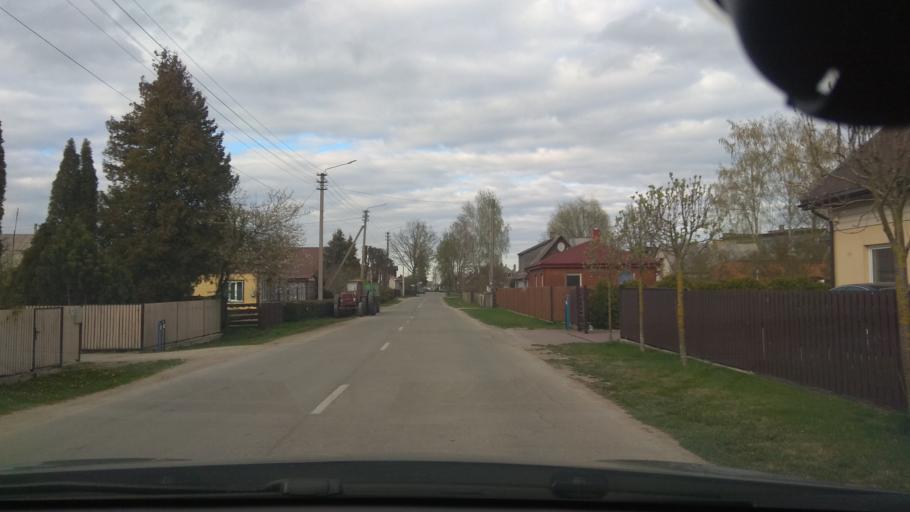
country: LT
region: Siauliu apskritis
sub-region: Joniskis
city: Joniskis
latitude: 56.2465
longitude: 23.6139
